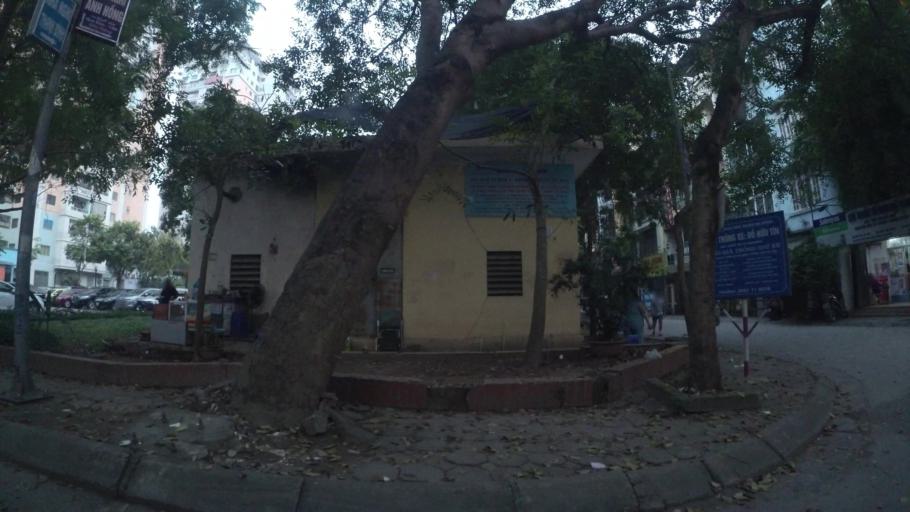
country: VN
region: Ha Noi
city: Ha Dong
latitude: 20.9725
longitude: 105.7885
